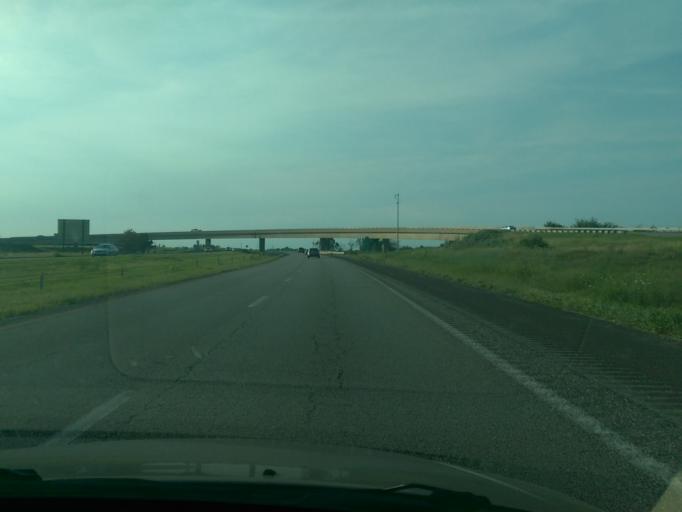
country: US
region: Missouri
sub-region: Platte County
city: Weatherby Lake
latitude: 39.3093
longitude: -94.6871
